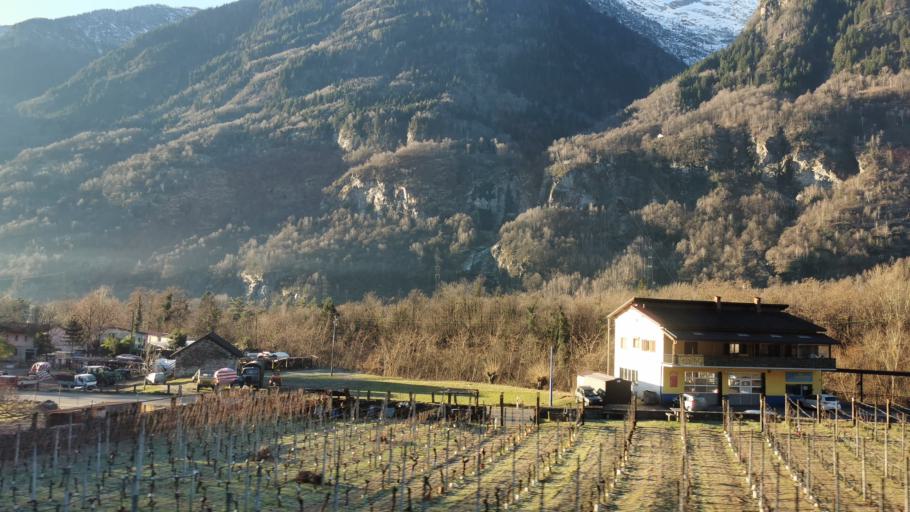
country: CH
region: Ticino
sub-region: Leventina District
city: Bodio
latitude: 46.3983
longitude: 8.8836
